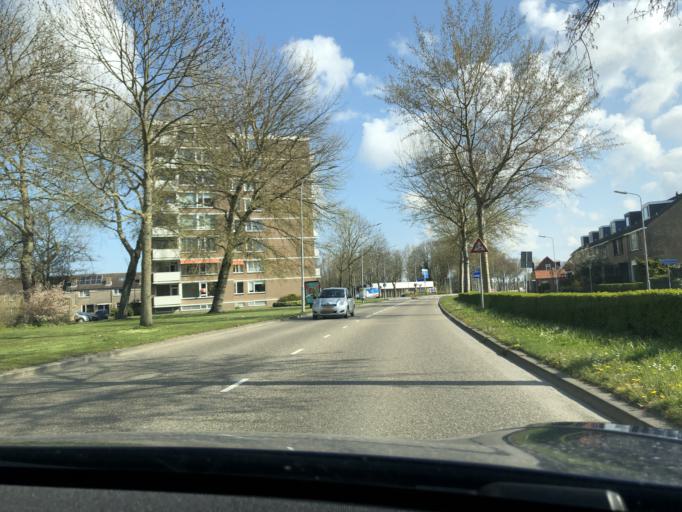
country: NL
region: Zeeland
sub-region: Gemeente Middelburg
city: Middelburg
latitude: 51.5047
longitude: 3.5973
